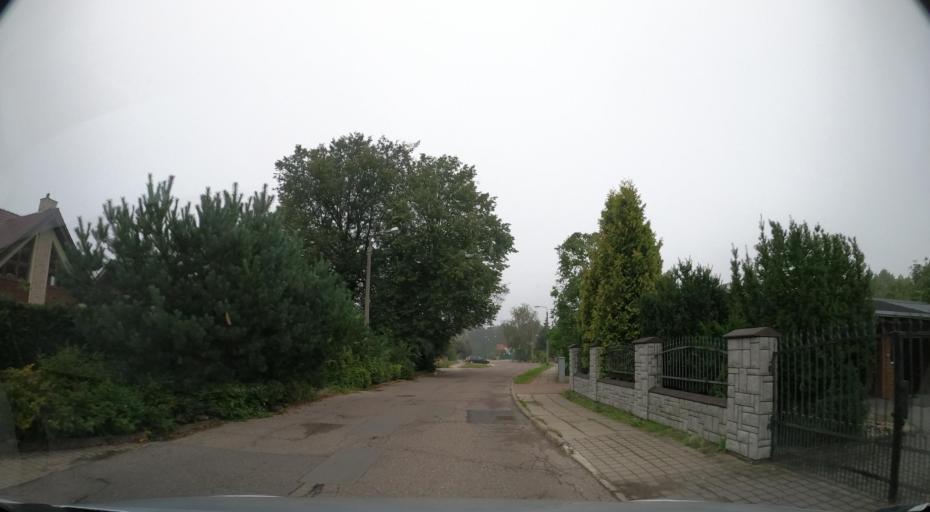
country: PL
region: Pomeranian Voivodeship
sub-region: Powiat kartuski
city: Chwaszczyno
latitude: 54.4253
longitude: 18.4619
